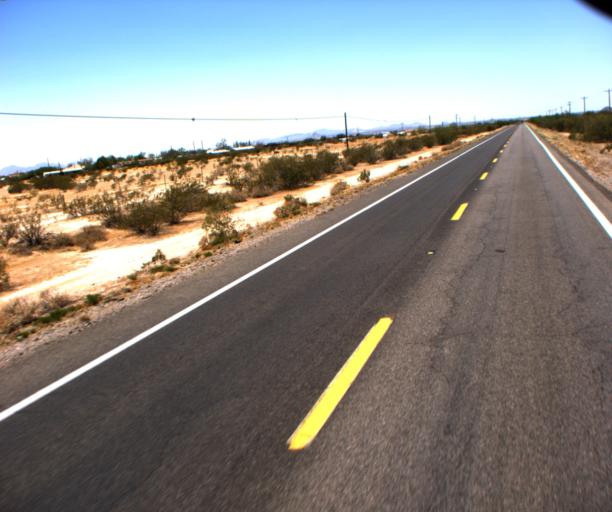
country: US
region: Arizona
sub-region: Pinal County
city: Florence
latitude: 32.9772
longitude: -111.3514
